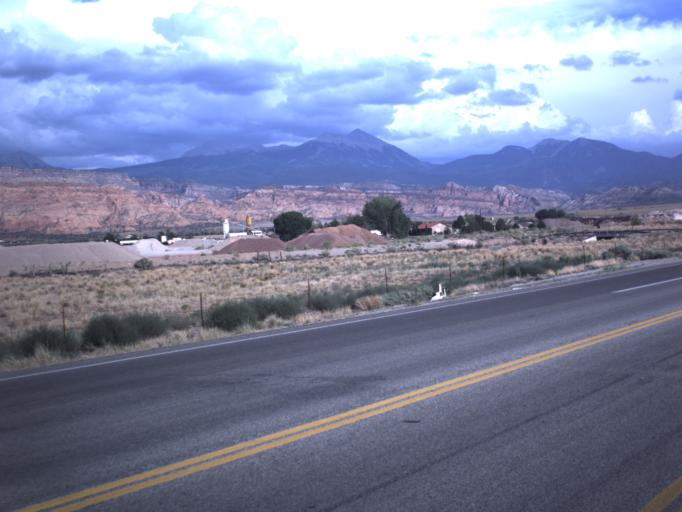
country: US
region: Utah
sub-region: Grand County
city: Moab
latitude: 38.4885
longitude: -109.4641
